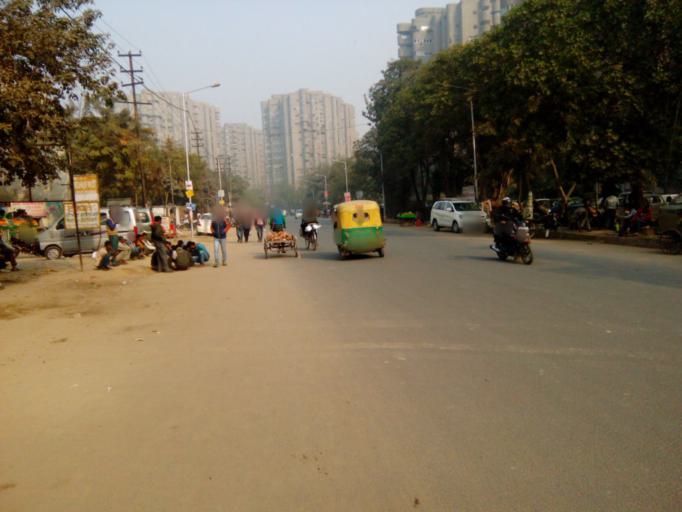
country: IN
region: Uttar Pradesh
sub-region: Gautam Buddha Nagar
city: Noida
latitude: 28.6415
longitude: 77.3195
